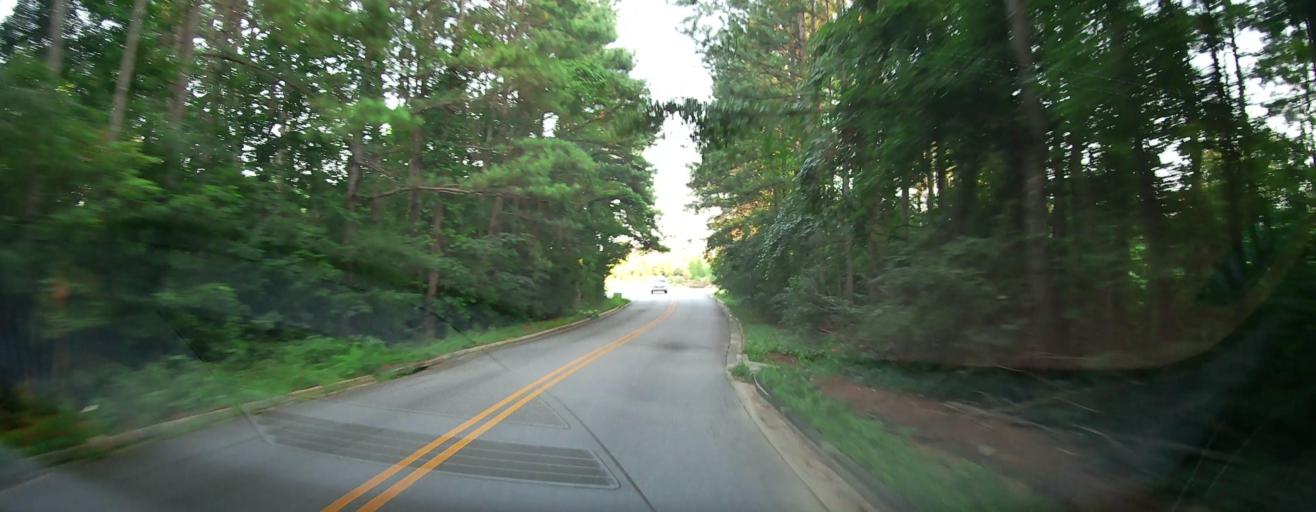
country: US
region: Georgia
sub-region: Bibb County
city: Macon
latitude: 32.9166
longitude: -83.7117
